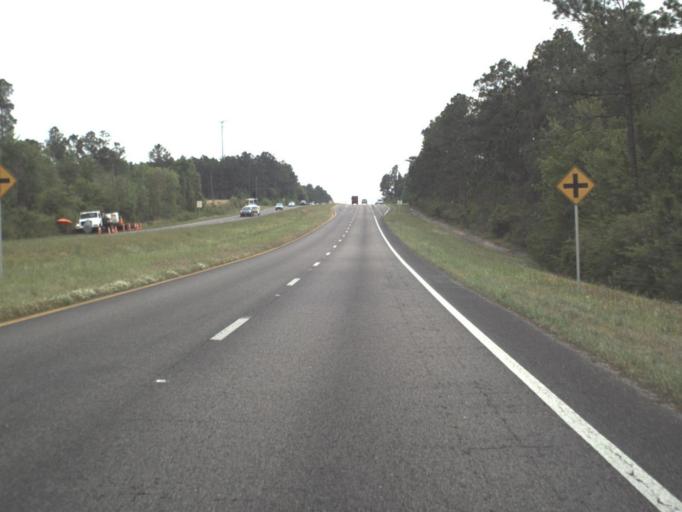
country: US
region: Florida
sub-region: Escambia County
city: Molino
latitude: 30.6836
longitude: -87.3511
